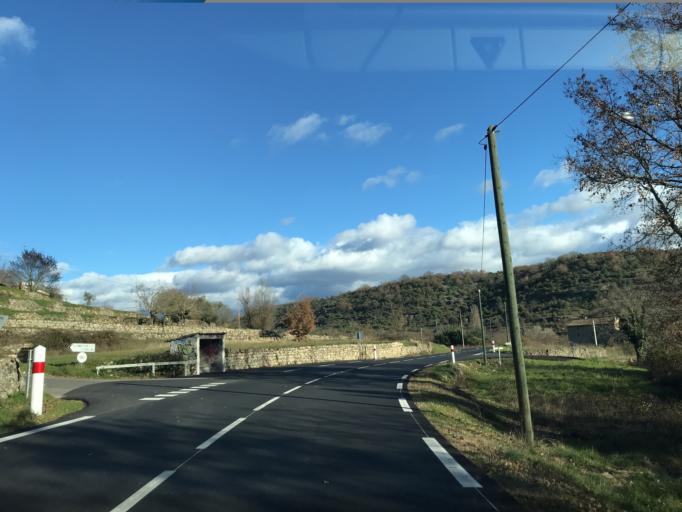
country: FR
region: Rhone-Alpes
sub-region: Departement de l'Ardeche
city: Les Vans
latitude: 44.4257
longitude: 4.1801
